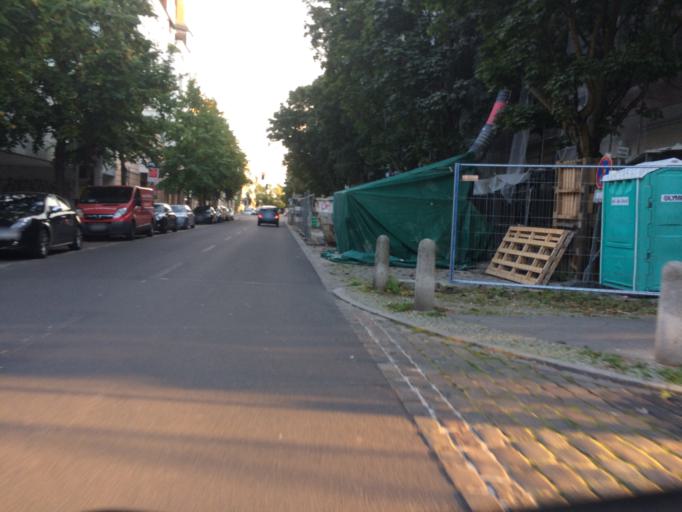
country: DE
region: Berlin
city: Gesundbrunnen
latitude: 52.5523
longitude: 13.4034
